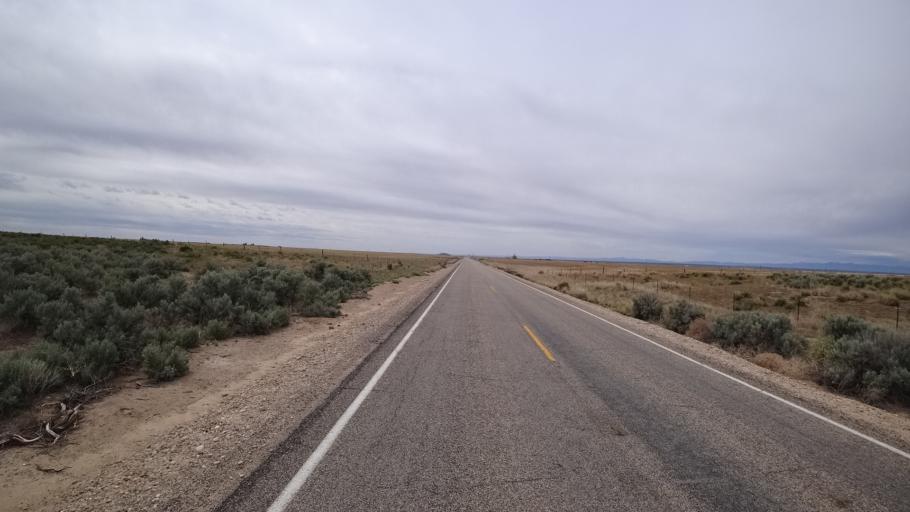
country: US
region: Idaho
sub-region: Ada County
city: Boise
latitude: 43.3584
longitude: -116.0049
